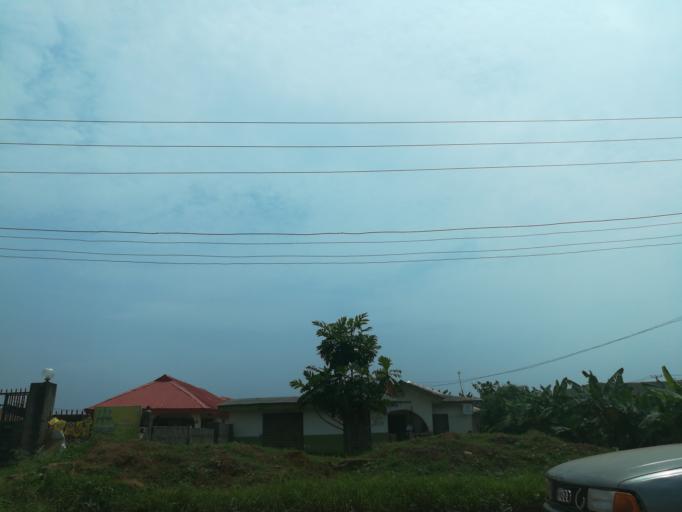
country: NG
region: Lagos
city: Ikorodu
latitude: 6.6048
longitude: 3.6008
